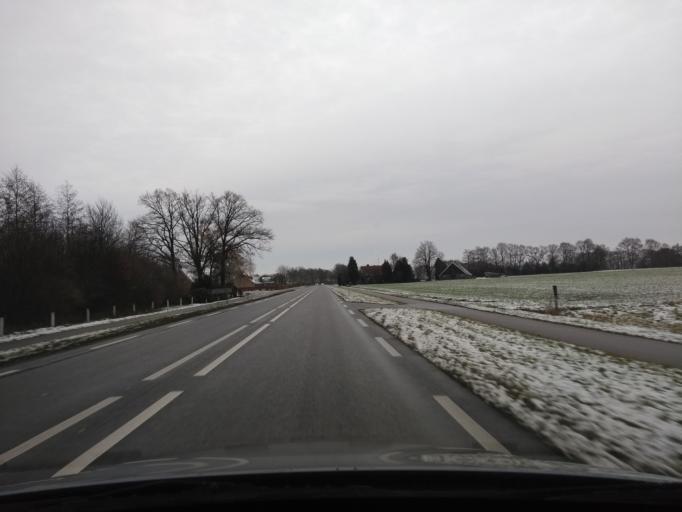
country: NL
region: Overijssel
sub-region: Gemeente Haaksbergen
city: Haaksbergen
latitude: 52.1993
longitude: 6.7322
